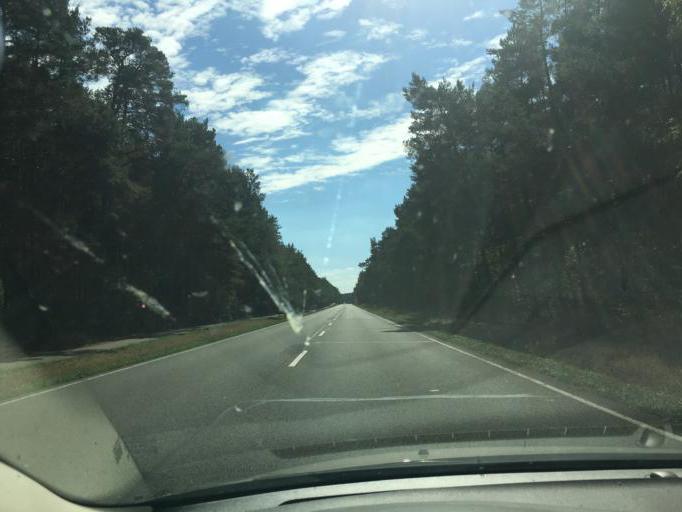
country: DE
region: Saxony-Anhalt
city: Seehausen
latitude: 52.8414
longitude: 11.7322
